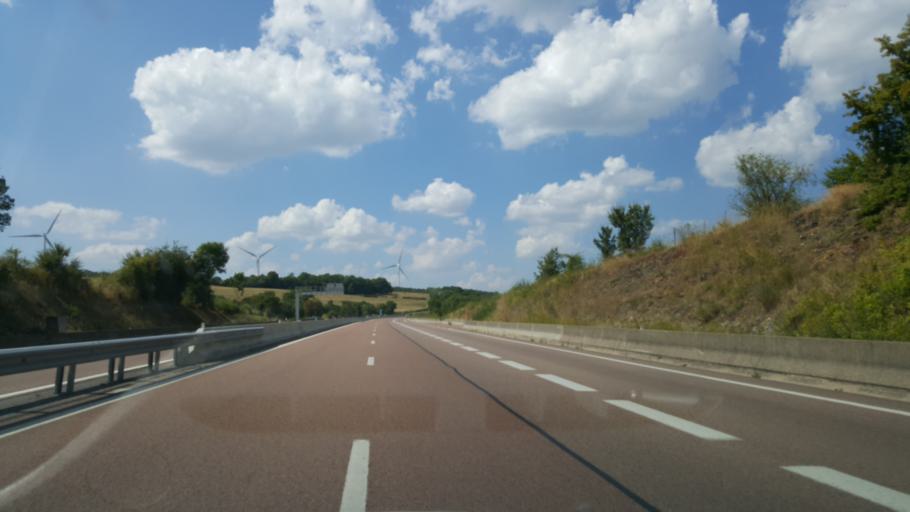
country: FR
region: Bourgogne
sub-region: Departement de la Cote-d'Or
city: Savigny-les-Beaune
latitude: 47.0875
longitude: 4.7570
